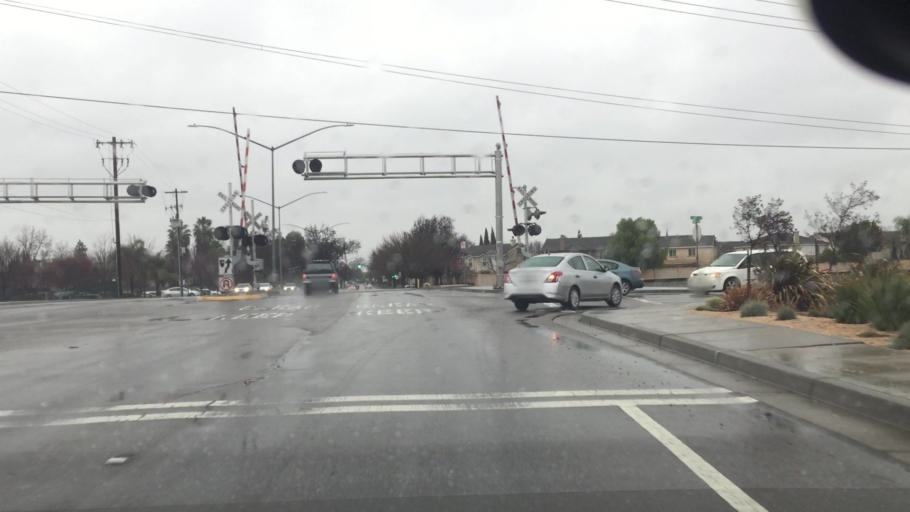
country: US
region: California
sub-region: San Joaquin County
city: Tracy
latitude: 37.7299
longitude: -121.4347
